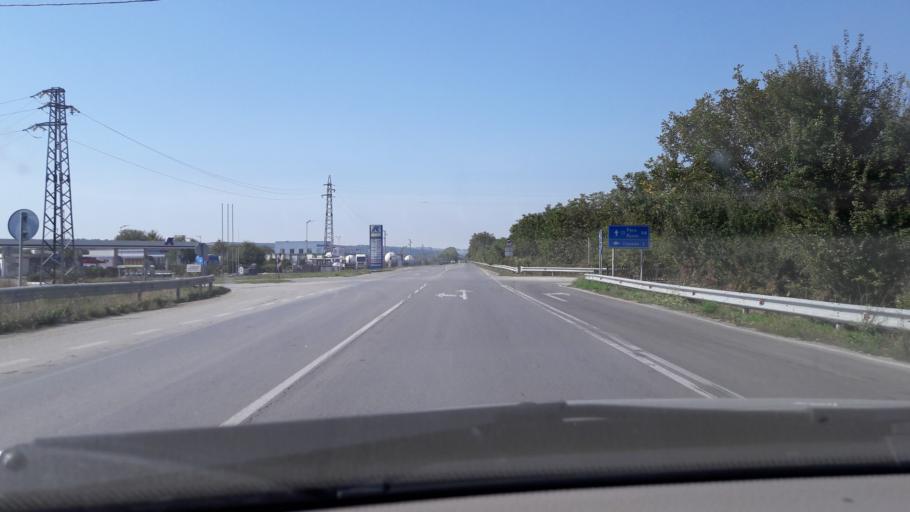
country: BG
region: Razgrad
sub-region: Obshtina Razgrad
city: Razgrad
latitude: 43.5483
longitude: 26.4794
